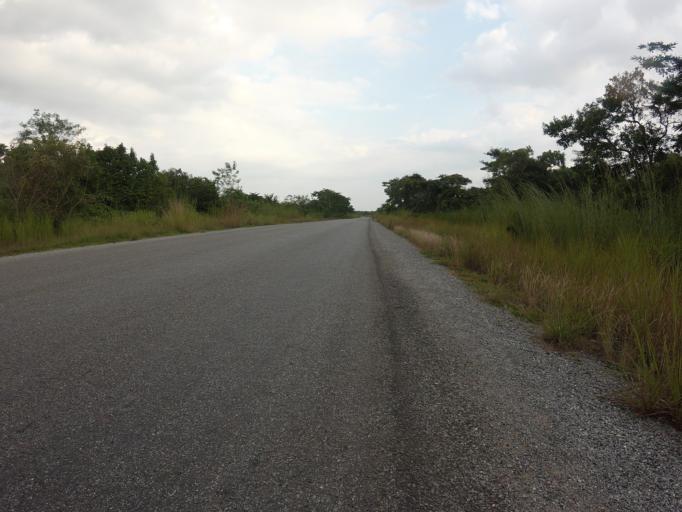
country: GH
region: Volta
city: Ho
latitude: 6.4353
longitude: 0.5054
